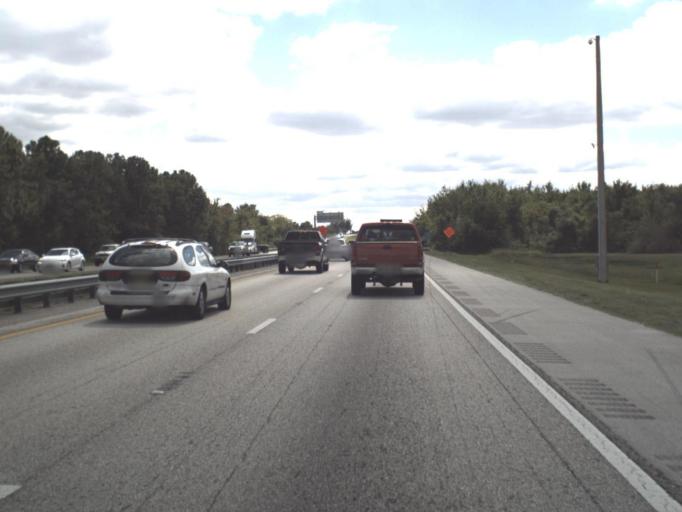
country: US
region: Florida
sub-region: Orange County
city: Southchase
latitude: 28.4128
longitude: -81.3917
